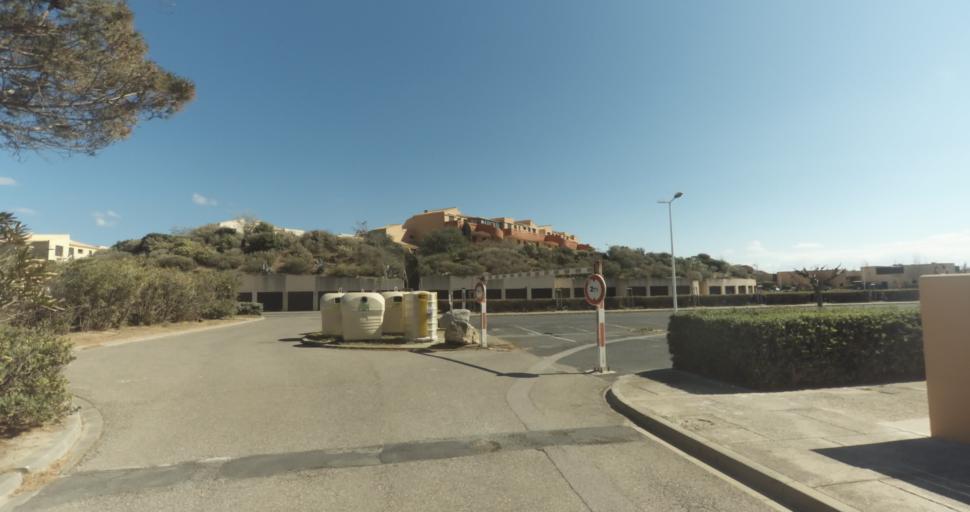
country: FR
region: Languedoc-Roussillon
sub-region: Departement de l'Aude
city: Leucate
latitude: 42.8545
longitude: 3.0426
